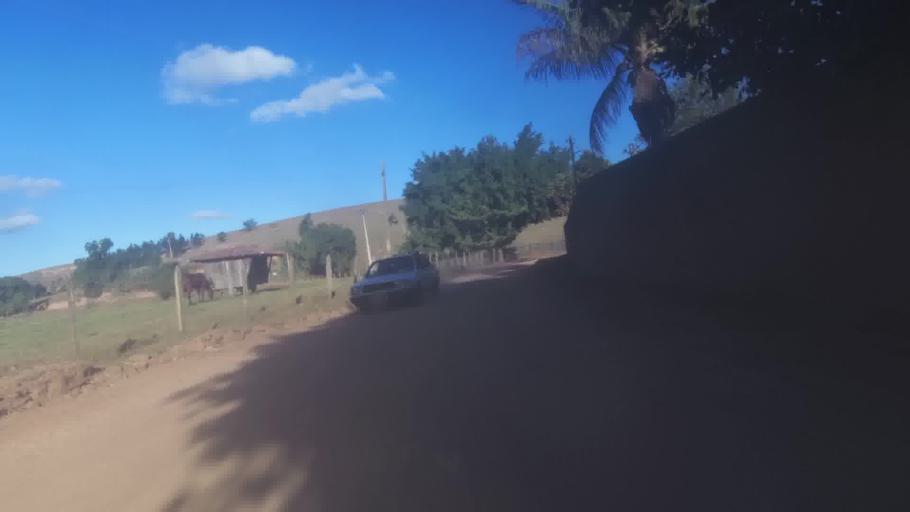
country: BR
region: Espirito Santo
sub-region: Mimoso Do Sul
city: Mimoso do Sul
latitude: -21.1025
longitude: -41.1293
